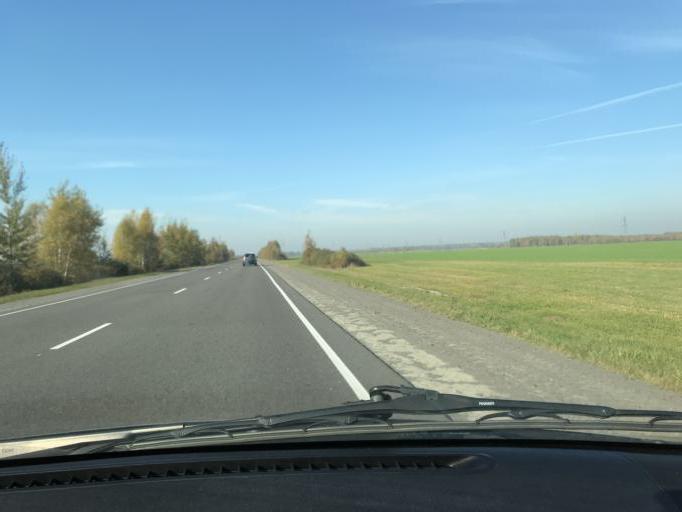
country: BY
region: Brest
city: Horad Luninyets
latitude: 52.3111
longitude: 26.6673
